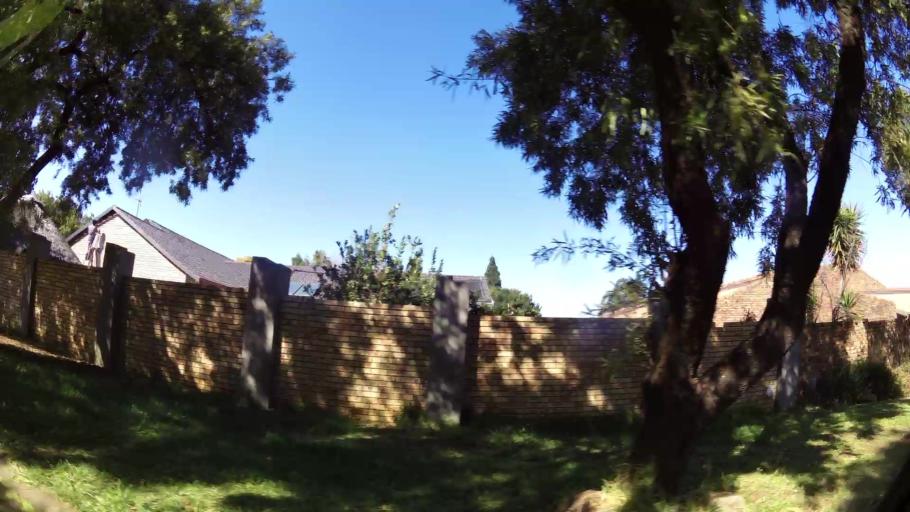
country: ZA
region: Gauteng
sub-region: Ekurhuleni Metropolitan Municipality
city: Germiston
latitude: -26.3003
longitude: 28.0956
